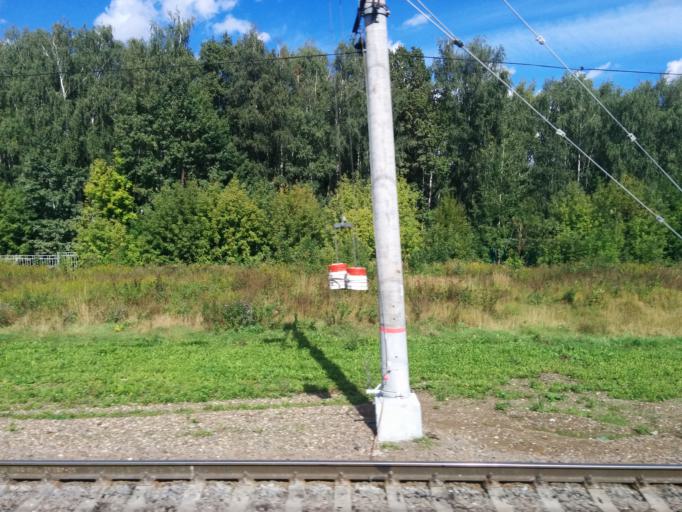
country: RU
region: Moskovskaya
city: Vostochnoe Degunino
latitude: 55.8936
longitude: 37.5635
